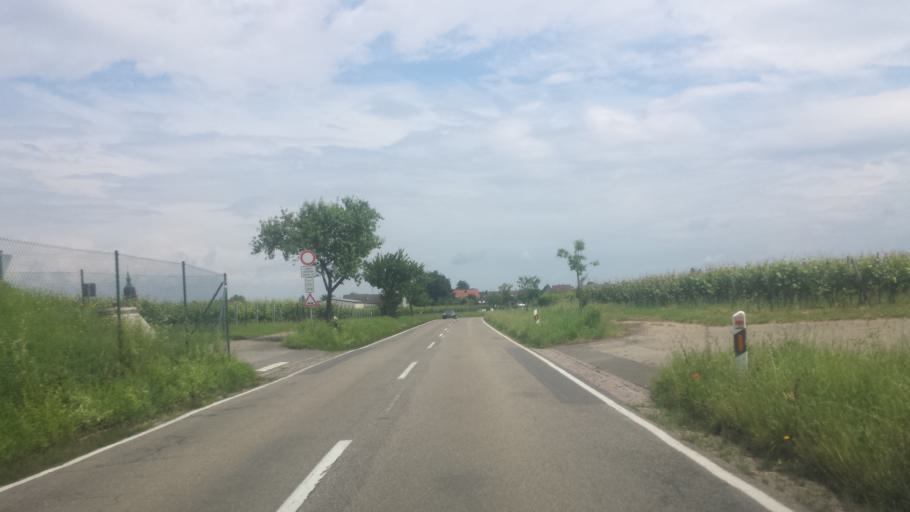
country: DE
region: Rheinland-Pfalz
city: Hainfeld
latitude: 49.2542
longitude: 8.0946
